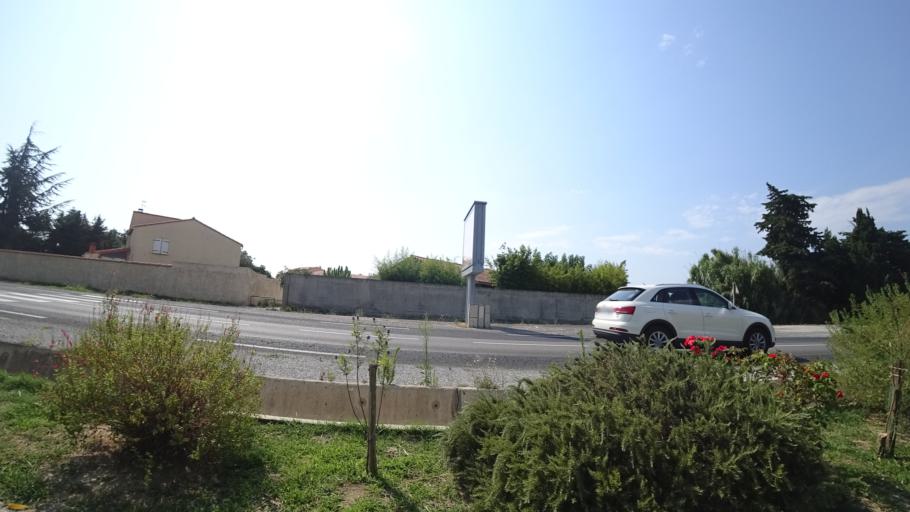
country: FR
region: Languedoc-Roussillon
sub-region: Departement des Pyrenees-Orientales
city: Bompas
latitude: 42.7216
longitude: 2.9348
